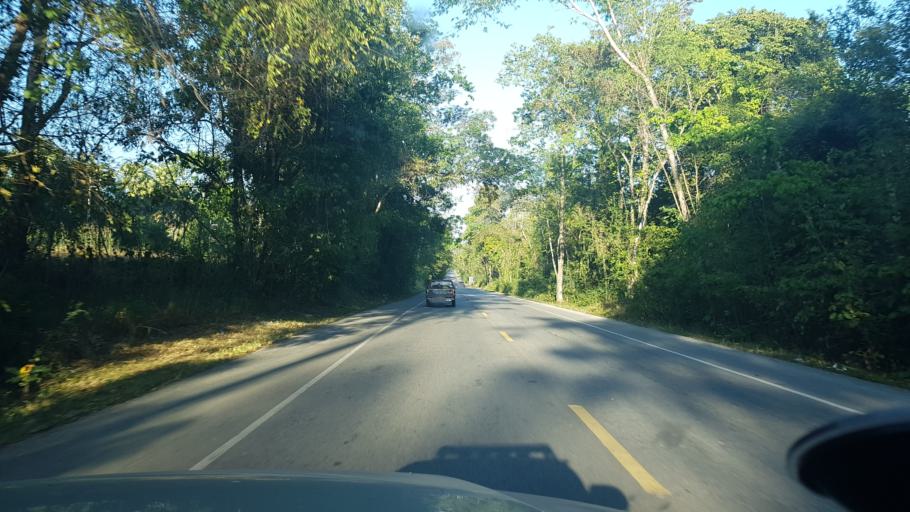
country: TH
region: Khon Kaen
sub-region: Amphoe Phu Pha Man
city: Phu Pha Man
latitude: 16.6271
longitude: 101.8483
